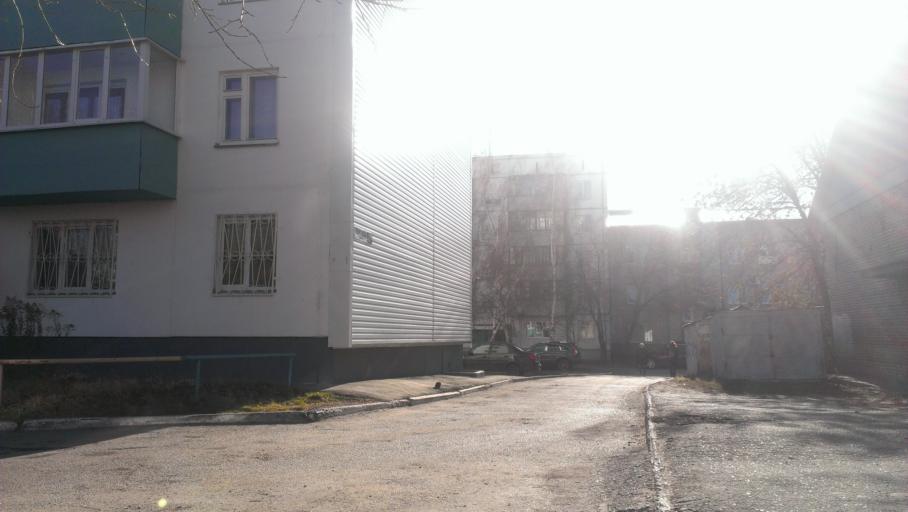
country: RU
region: Altai Krai
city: Novosilikatnyy
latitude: 53.3459
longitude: 83.6873
